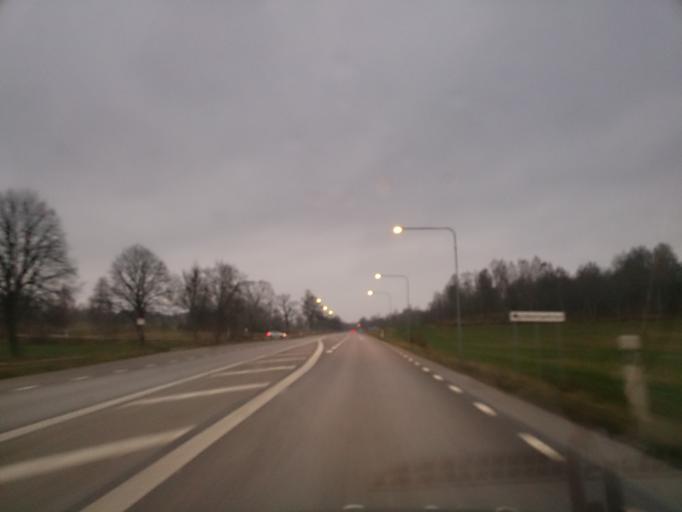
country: SE
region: OEstergoetland
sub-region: Atvidabergs Kommun
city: Atvidaberg
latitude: 58.2265
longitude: 15.9674
